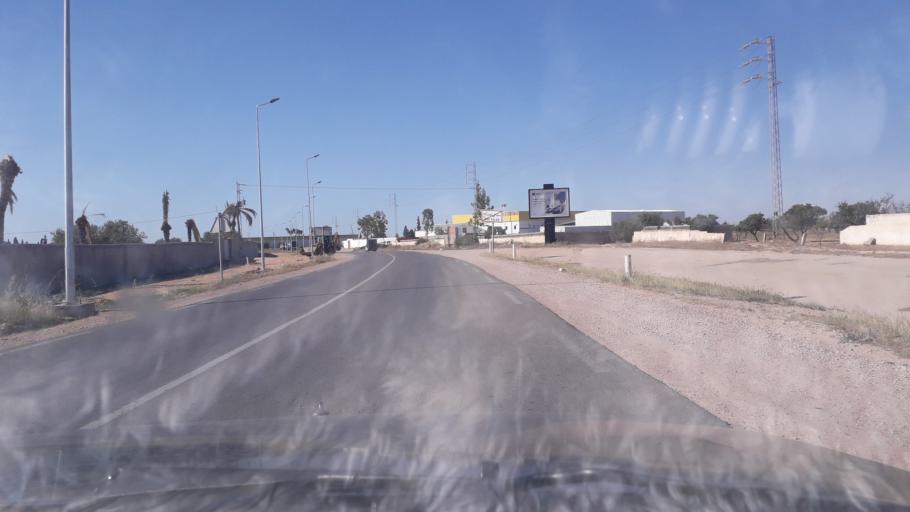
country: TN
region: Safaqis
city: Al Qarmadah
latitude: 34.8749
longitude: 10.7562
